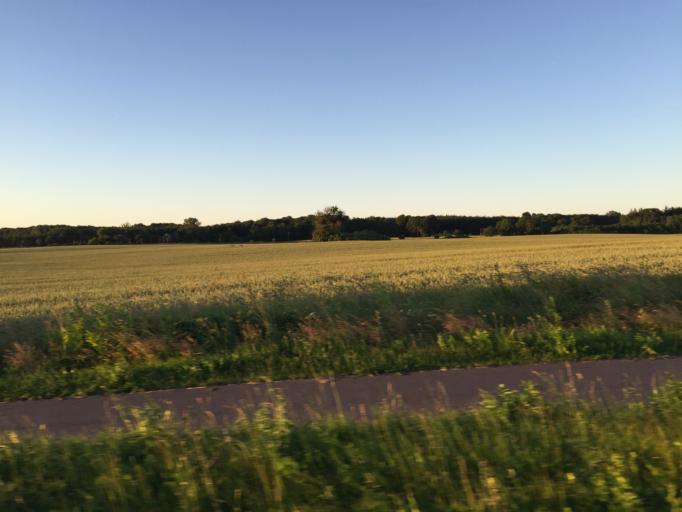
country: DK
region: South Denmark
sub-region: Nyborg Kommune
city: Nyborg
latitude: 55.3262
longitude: 10.7639
